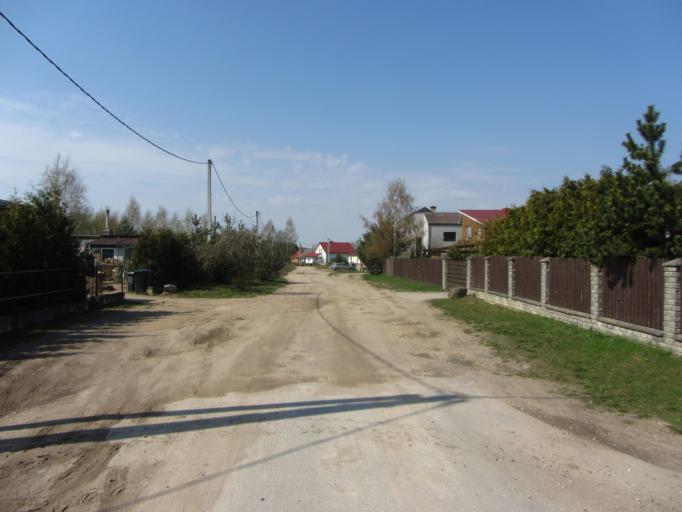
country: LT
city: Lentvaris
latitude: 54.6394
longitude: 25.0281
